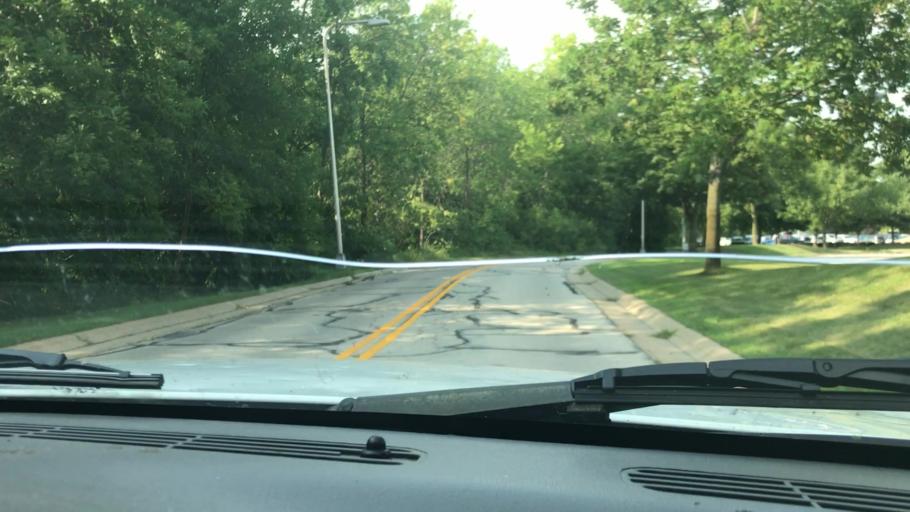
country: US
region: Wisconsin
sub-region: Brown County
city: Bellevue
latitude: 44.5346
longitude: -87.9263
